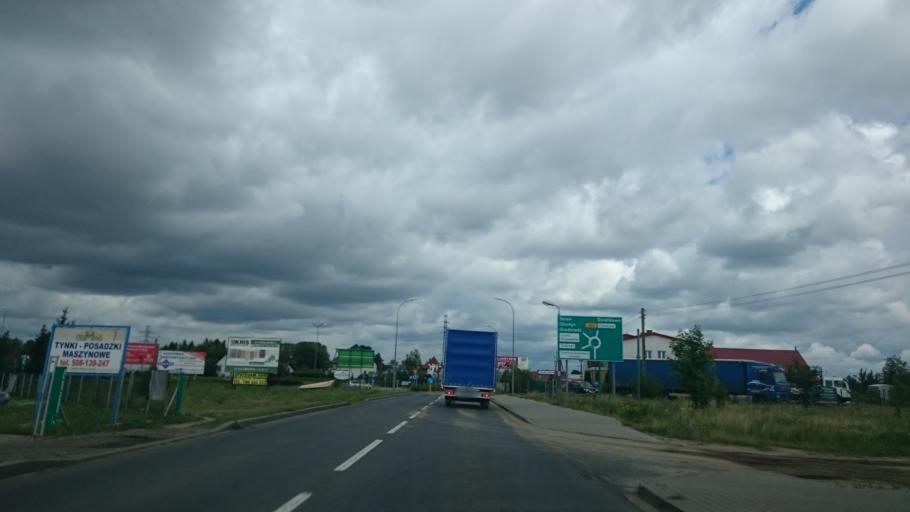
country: PL
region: Kujawsko-Pomorskie
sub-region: Powiat brodnicki
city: Brodnica
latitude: 53.2340
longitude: 19.3903
